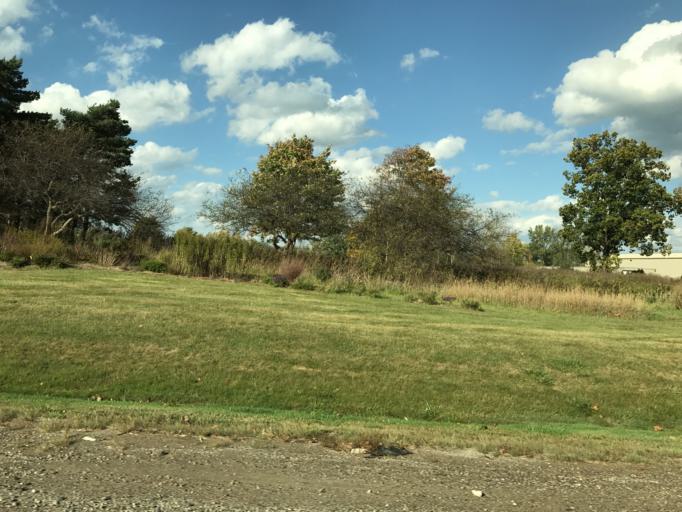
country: US
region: Michigan
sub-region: Oakland County
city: Wixom
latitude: 42.5031
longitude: -83.5758
